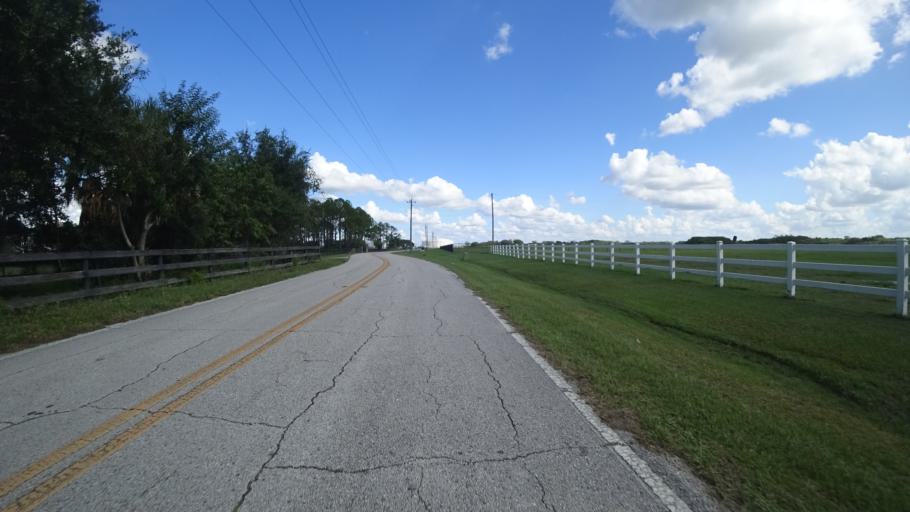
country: US
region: Florida
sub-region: Sarasota County
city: The Meadows
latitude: 27.4877
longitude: -82.3630
